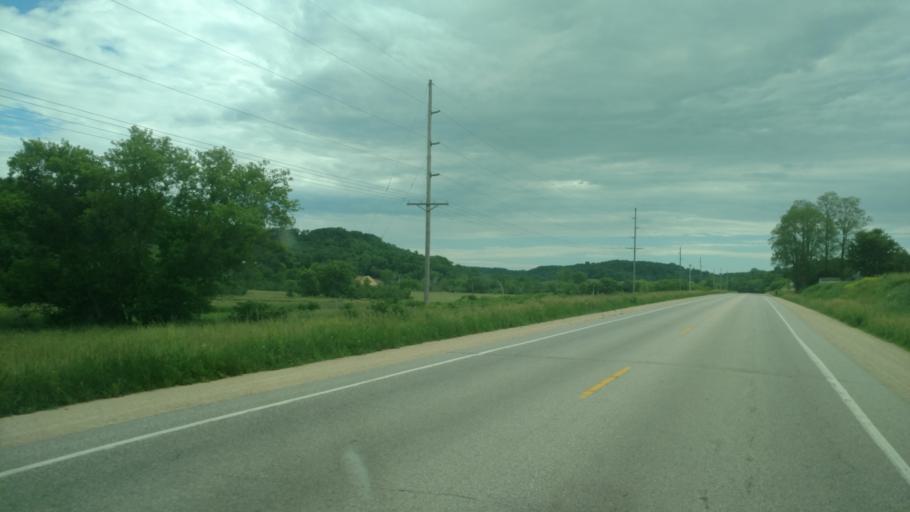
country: US
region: Wisconsin
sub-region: Monroe County
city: Tomah
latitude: 43.8279
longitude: -90.4592
